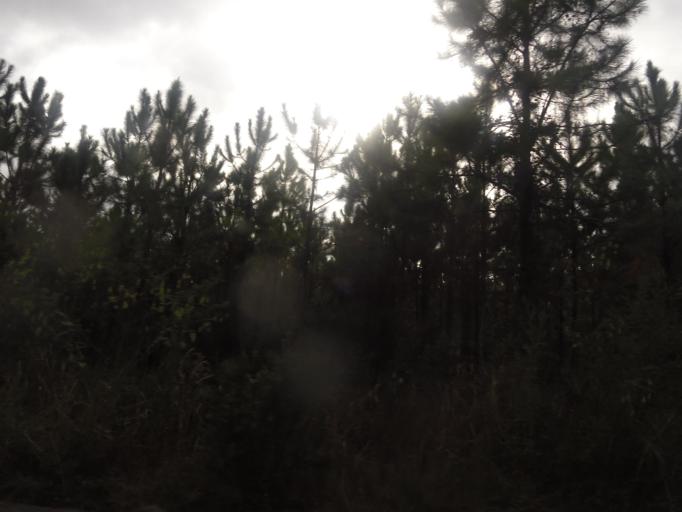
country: US
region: Florida
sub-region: Flagler County
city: Bunnell
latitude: 29.5505
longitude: -81.3276
